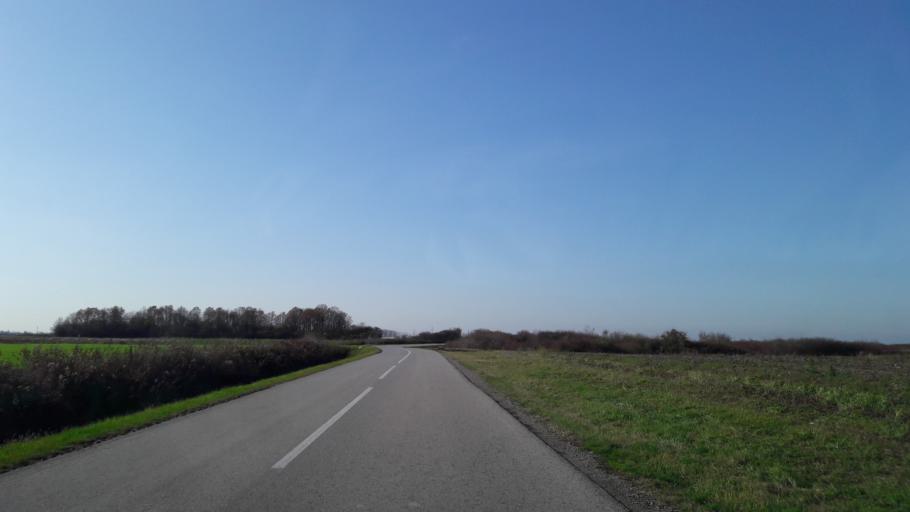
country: HR
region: Osjecko-Baranjska
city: Antunovac
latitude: 45.4762
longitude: 18.6991
